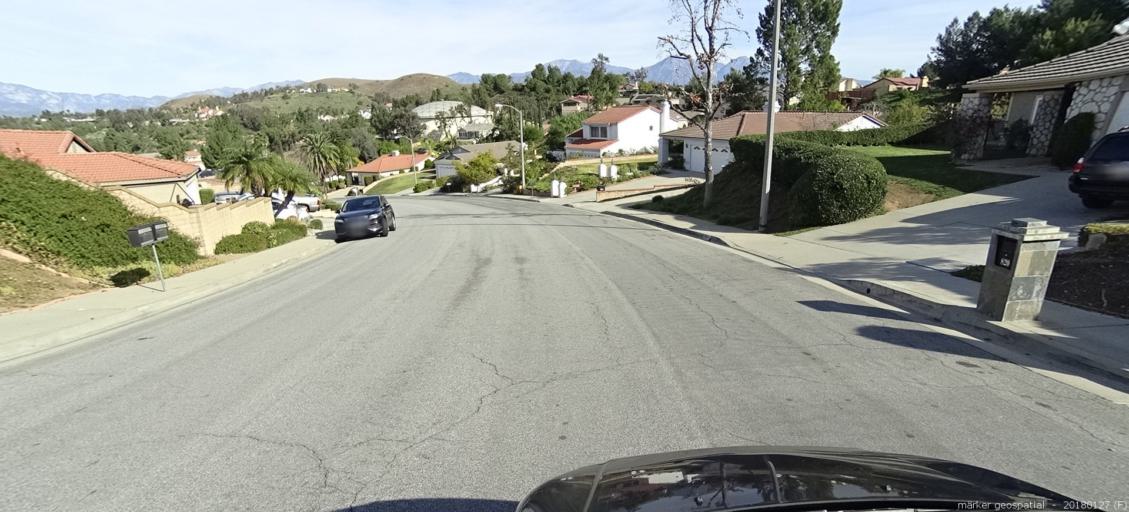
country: US
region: California
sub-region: Los Angeles County
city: Diamond Bar
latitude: 34.0303
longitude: -117.7879
